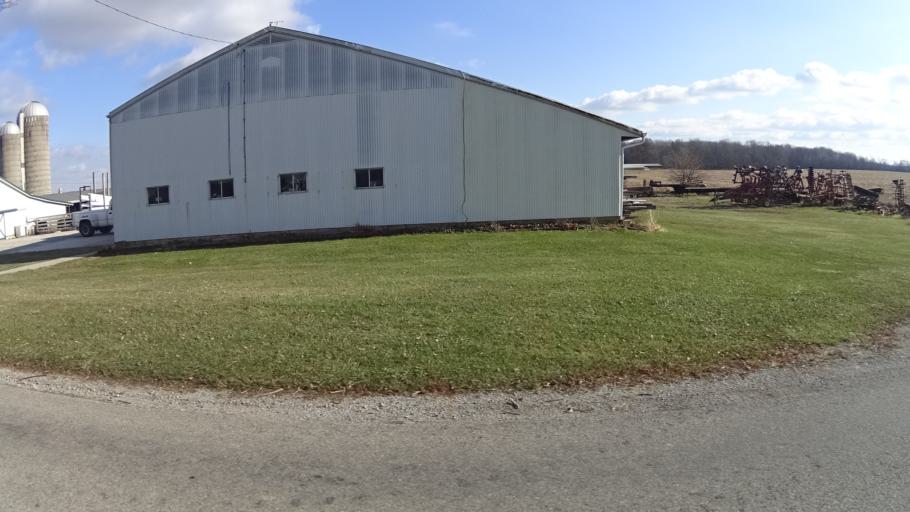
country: US
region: Ohio
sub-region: Lorain County
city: Camden
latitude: 41.2451
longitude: -82.2892
